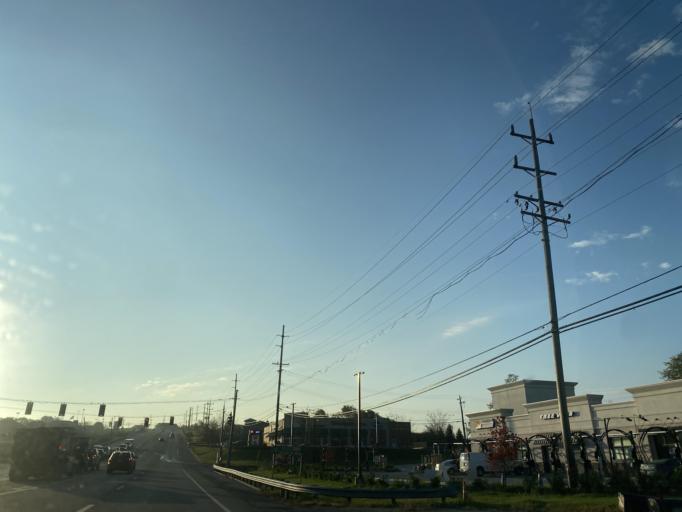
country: US
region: Kentucky
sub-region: Campbell County
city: Alexandria
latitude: 38.9862
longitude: -84.4037
